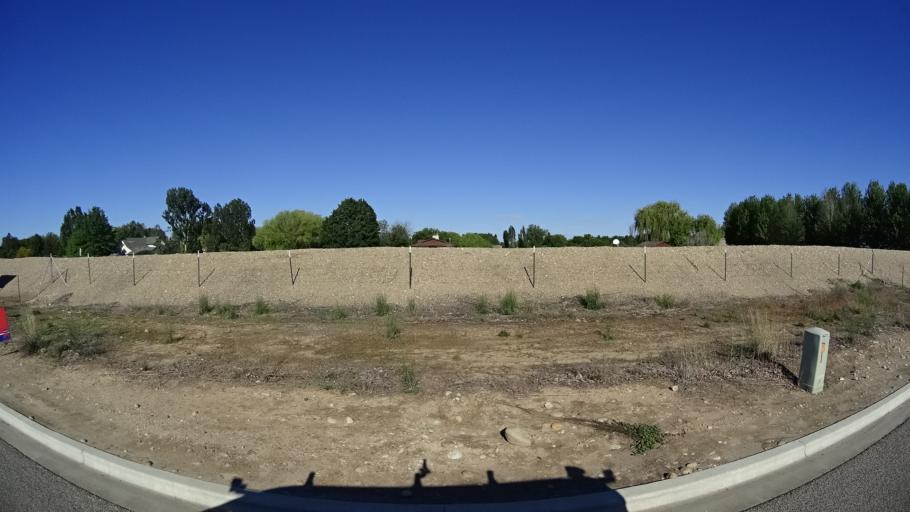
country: US
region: Idaho
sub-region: Ada County
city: Meridian
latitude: 43.6679
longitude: -116.4138
